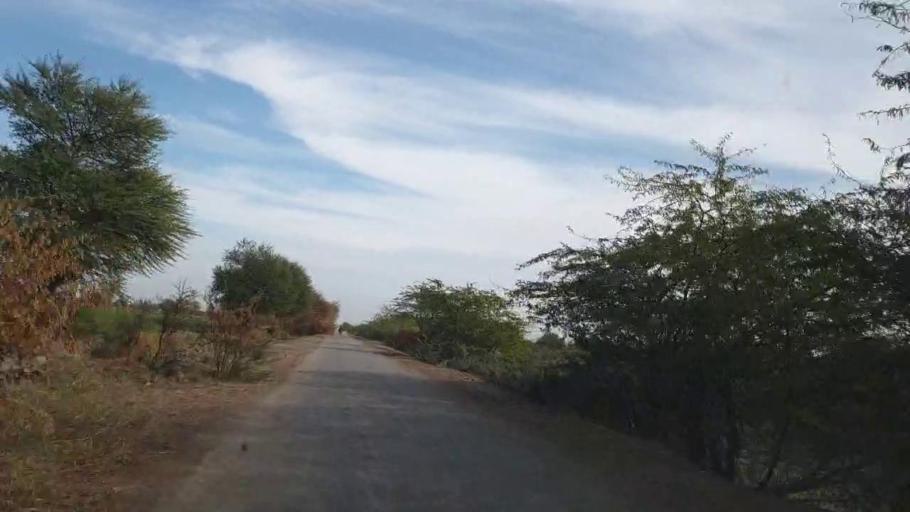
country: PK
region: Sindh
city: Pithoro
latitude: 25.6309
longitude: 69.4059
